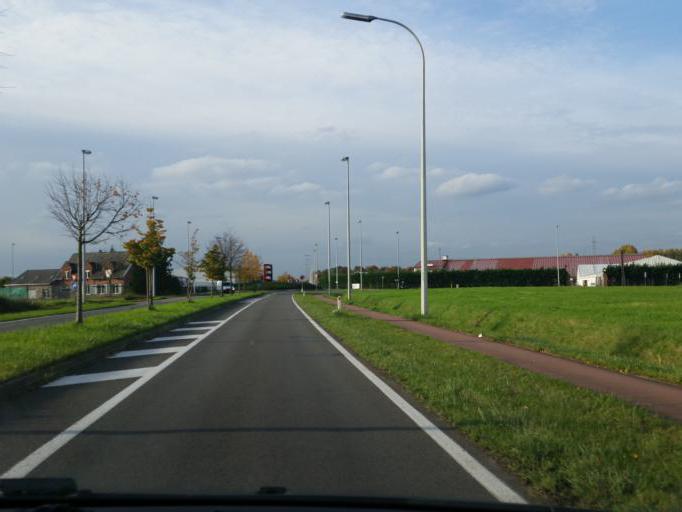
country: BE
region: Flanders
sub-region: Provincie Antwerpen
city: Putte
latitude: 51.0930
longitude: 4.6246
